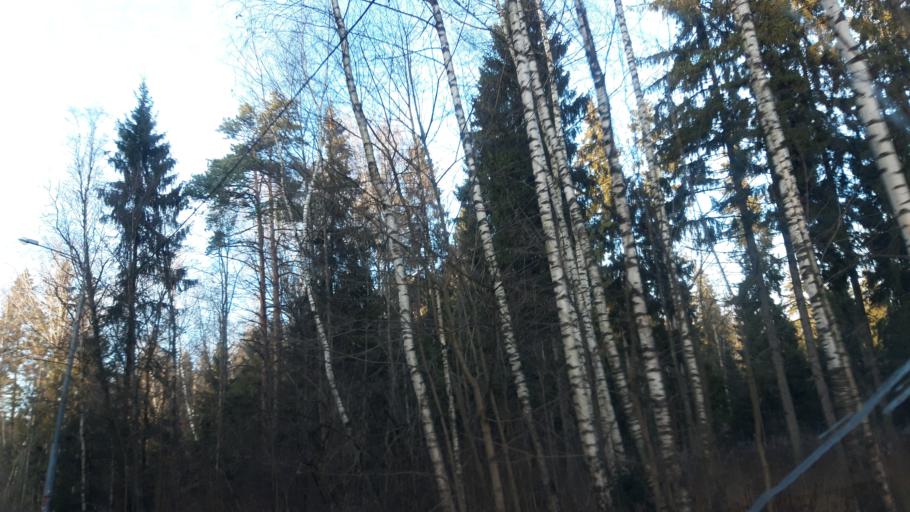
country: RU
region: Moskovskaya
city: Rzhavki
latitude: 55.9993
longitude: 37.2286
